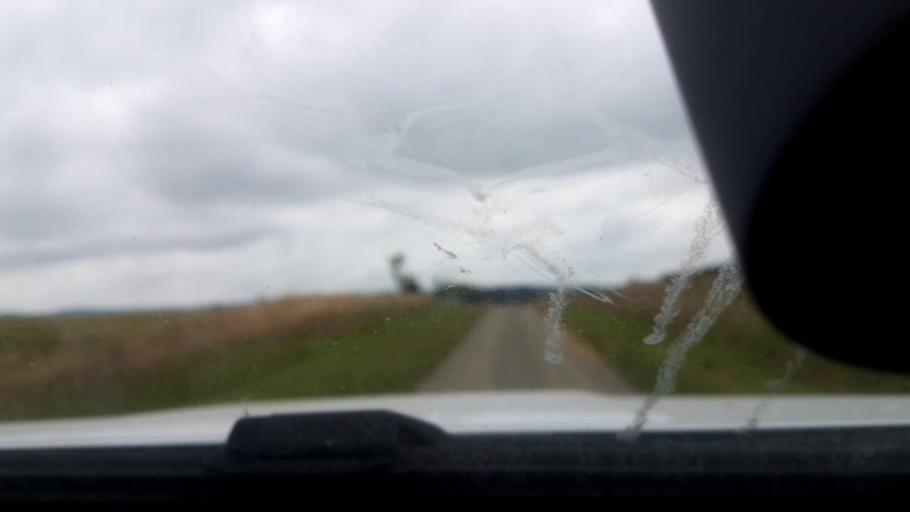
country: NZ
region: Canterbury
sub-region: Timaru District
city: Pleasant Point
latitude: -44.2285
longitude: 171.1656
